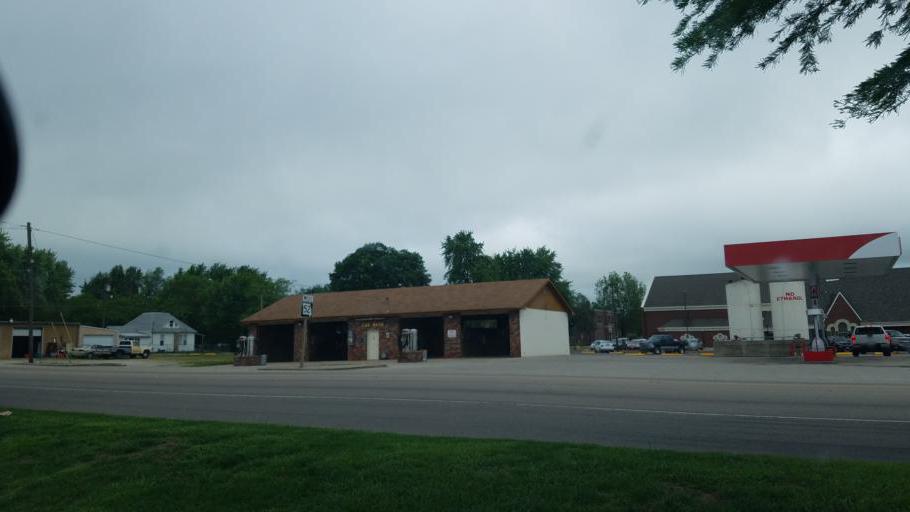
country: US
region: Missouri
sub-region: Miller County
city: Eldon
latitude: 38.3467
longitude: -92.5818
